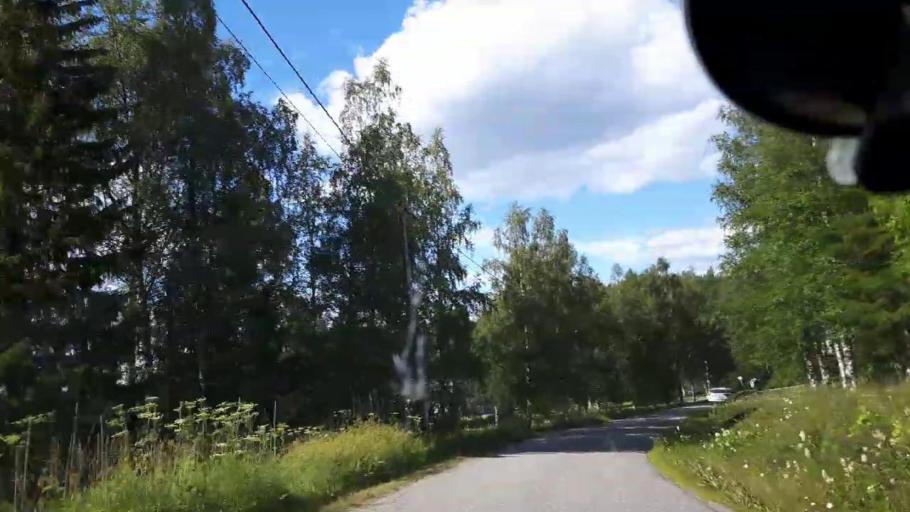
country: SE
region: Jaemtland
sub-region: Braecke Kommun
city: Braecke
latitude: 62.8854
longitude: 15.2723
